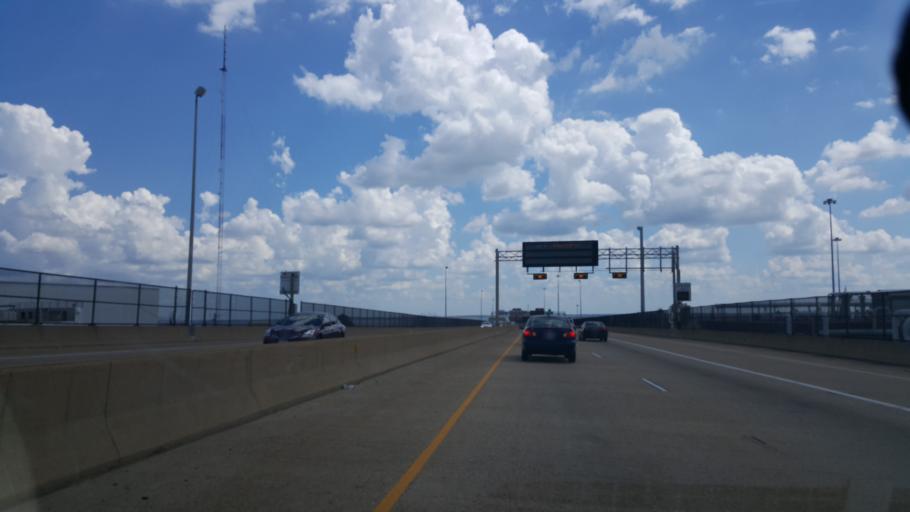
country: US
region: Virginia
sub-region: City of Newport News
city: Newport News
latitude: 36.9654
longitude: -76.4137
